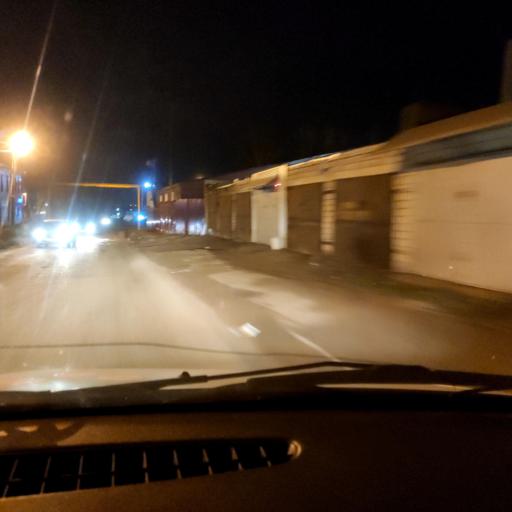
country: RU
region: Bashkortostan
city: Avdon
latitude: 54.6889
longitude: 55.8008
